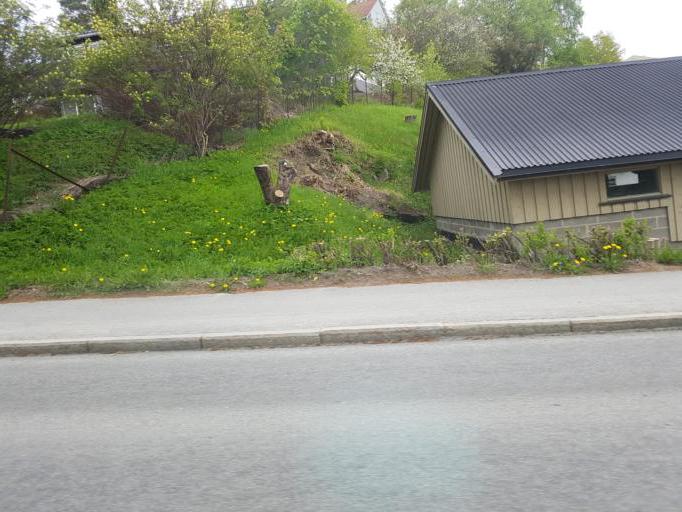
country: NO
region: Nord-Trondelag
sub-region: Levanger
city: Levanger
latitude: 63.7473
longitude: 11.2779
